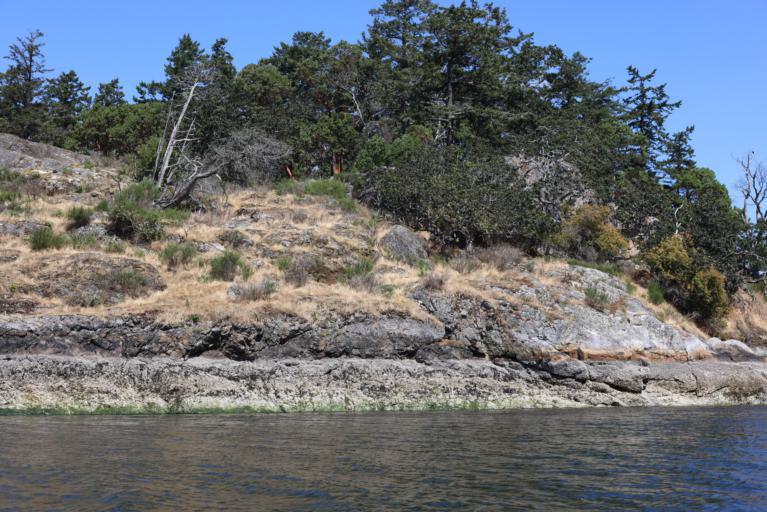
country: CA
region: British Columbia
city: Colwood
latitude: 48.4422
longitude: -123.4363
